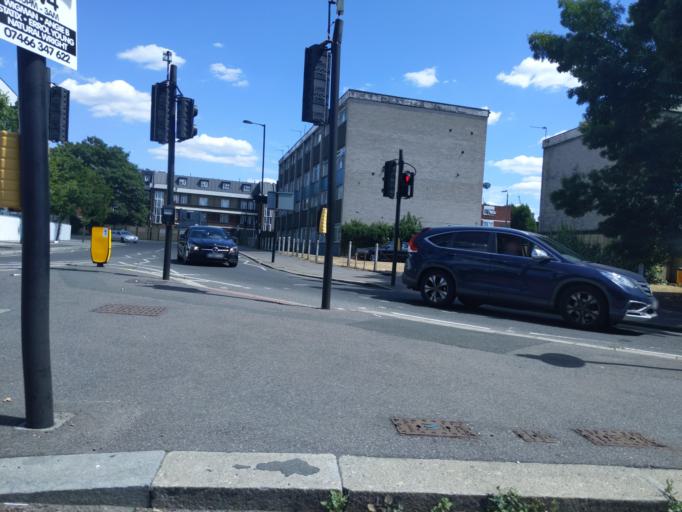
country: GB
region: England
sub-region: Greater London
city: Croydon
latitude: 51.3819
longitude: -0.0989
